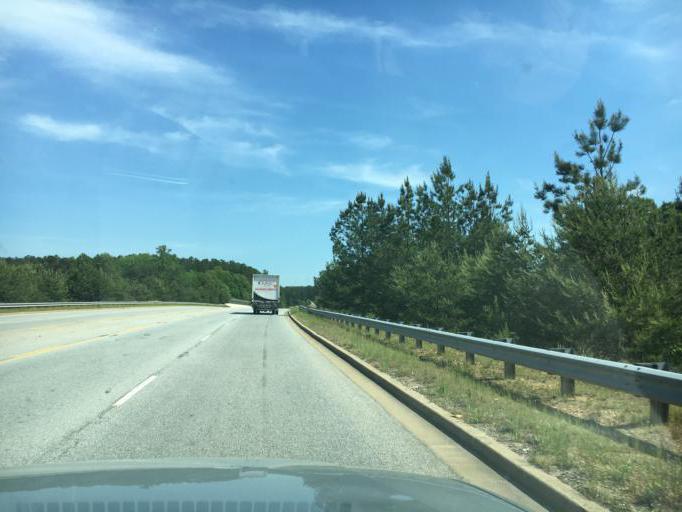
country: US
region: South Carolina
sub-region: Cherokee County
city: Blacksburg
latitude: 35.1292
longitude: -81.5062
